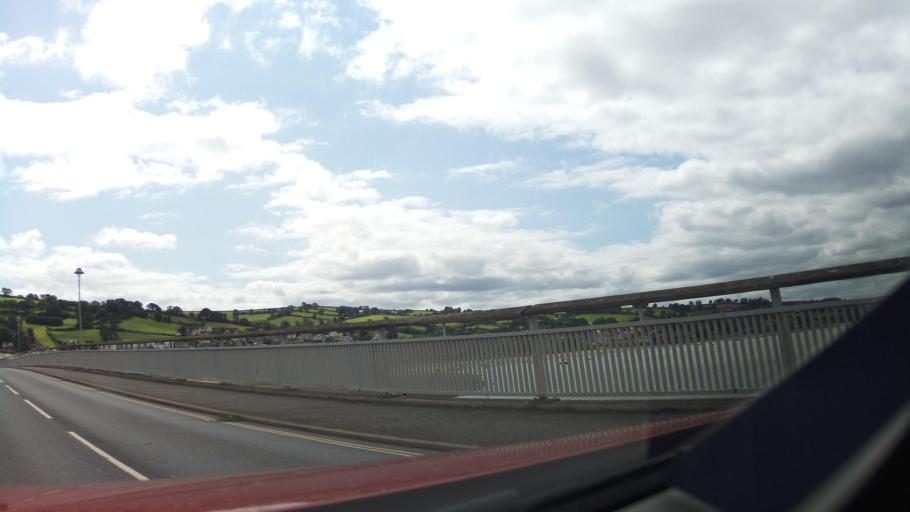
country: GB
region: England
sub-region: Devon
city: Teignmouth
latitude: 50.5458
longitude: -3.5104
